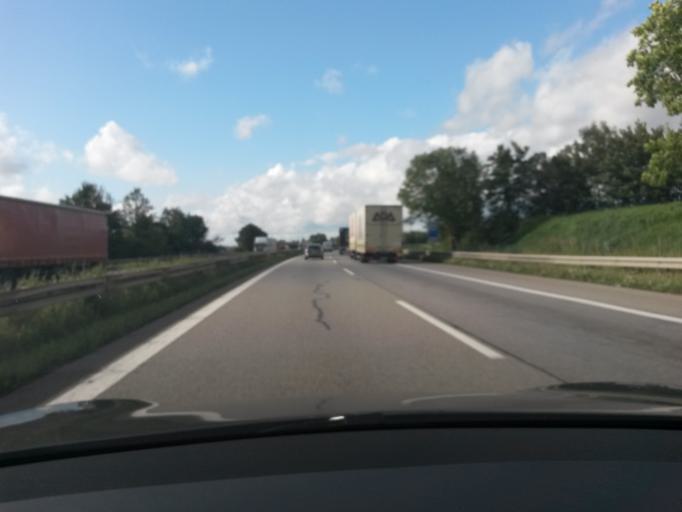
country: DE
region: Bavaria
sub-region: Upper Palatinate
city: Nittendorf
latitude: 49.0375
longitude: 11.9334
